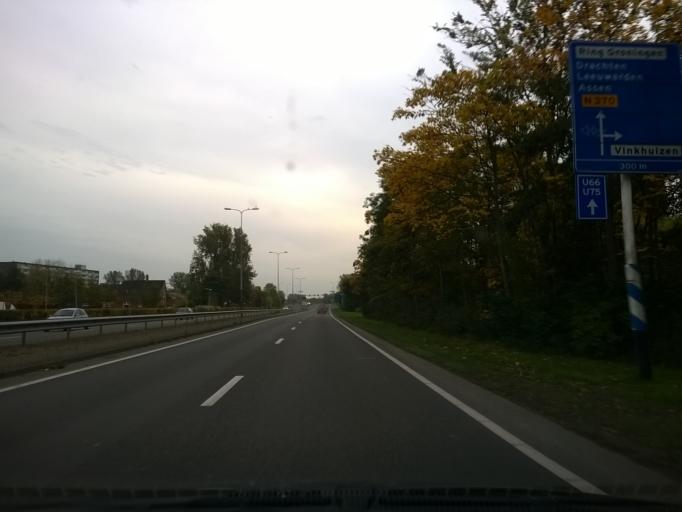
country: NL
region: Groningen
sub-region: Gemeente Groningen
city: Korrewegwijk
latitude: 53.2300
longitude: 6.5315
